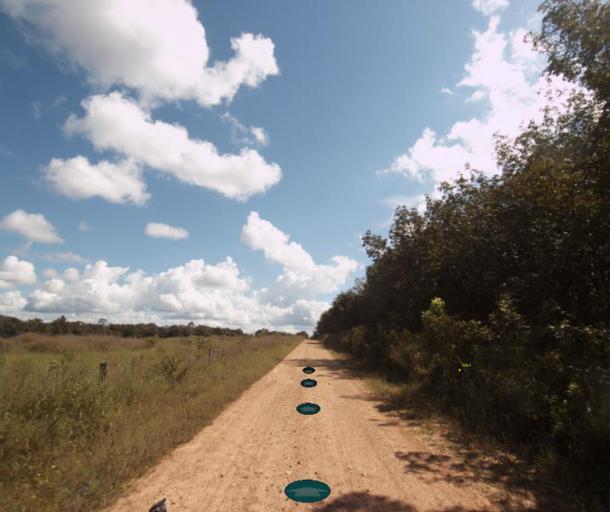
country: BR
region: Goias
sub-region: Pirenopolis
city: Pirenopolis
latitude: -15.7796
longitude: -49.0425
